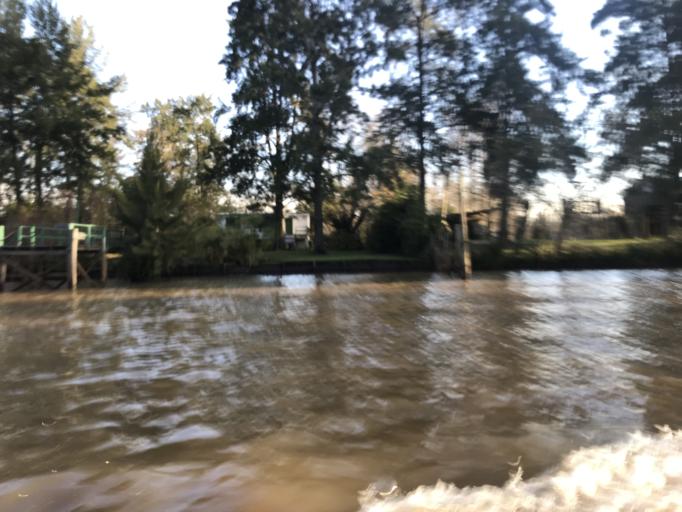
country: AR
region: Buenos Aires
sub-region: Partido de Tigre
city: Tigre
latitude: -34.3720
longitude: -58.5900
